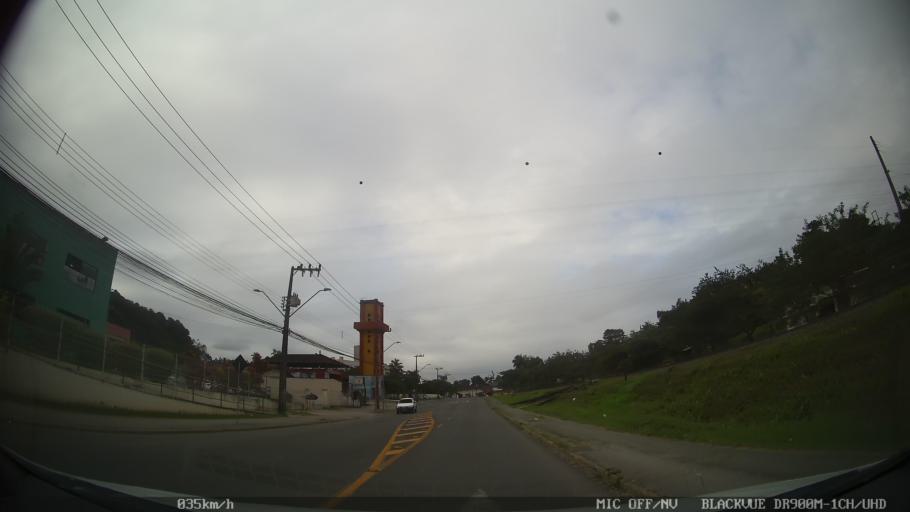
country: BR
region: Santa Catarina
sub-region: Joinville
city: Joinville
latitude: -26.3322
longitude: -48.8750
